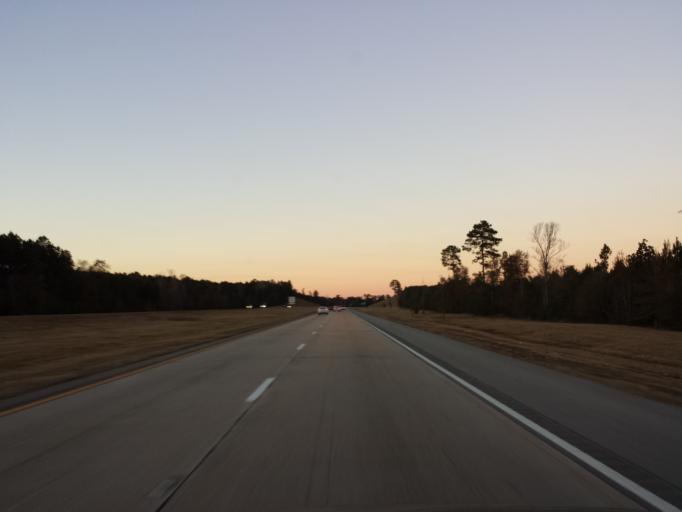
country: US
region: Mississippi
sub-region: Forrest County
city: Rawls Springs
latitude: 31.4776
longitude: -89.3233
